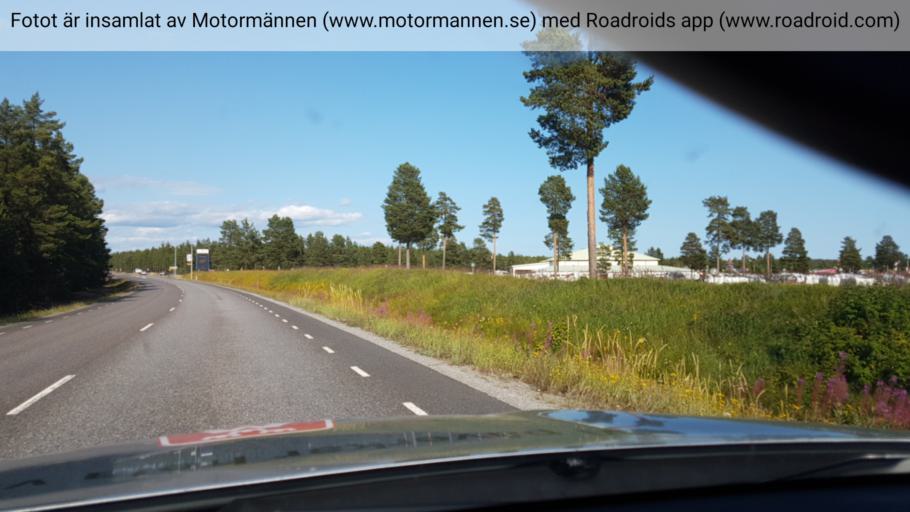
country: SE
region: Norrbotten
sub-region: Pitea Kommun
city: Pitea
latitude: 65.2345
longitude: 21.5232
